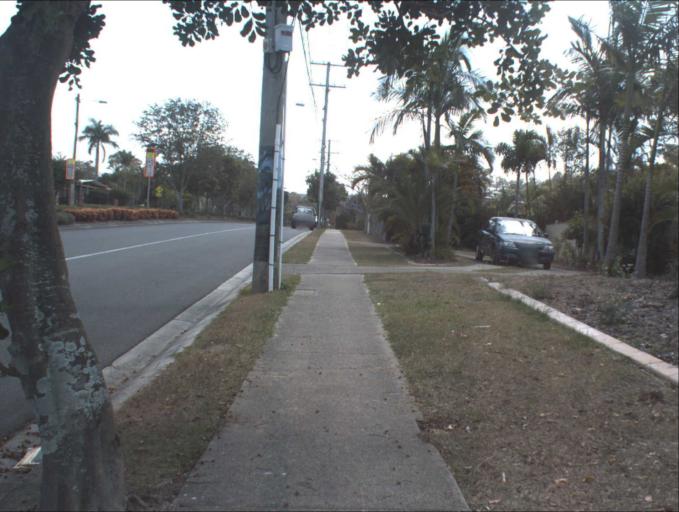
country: AU
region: Queensland
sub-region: Logan
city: Slacks Creek
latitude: -27.6636
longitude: 153.1847
